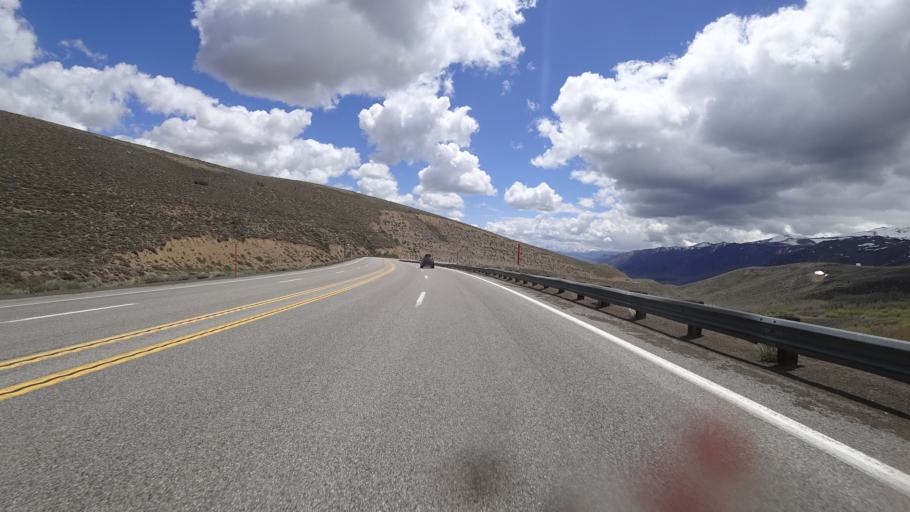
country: US
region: California
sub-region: Mono County
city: Bridgeport
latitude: 38.0862
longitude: -119.1815
